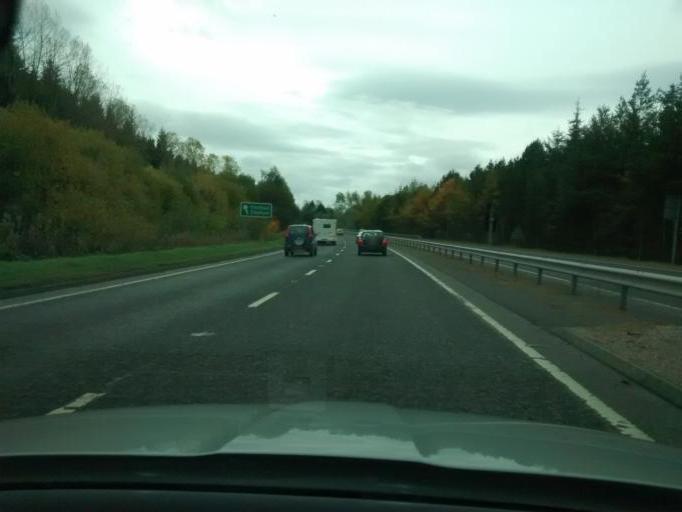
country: GB
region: Scotland
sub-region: Perth and Kinross
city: Luncarty
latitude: 56.4130
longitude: -3.4785
